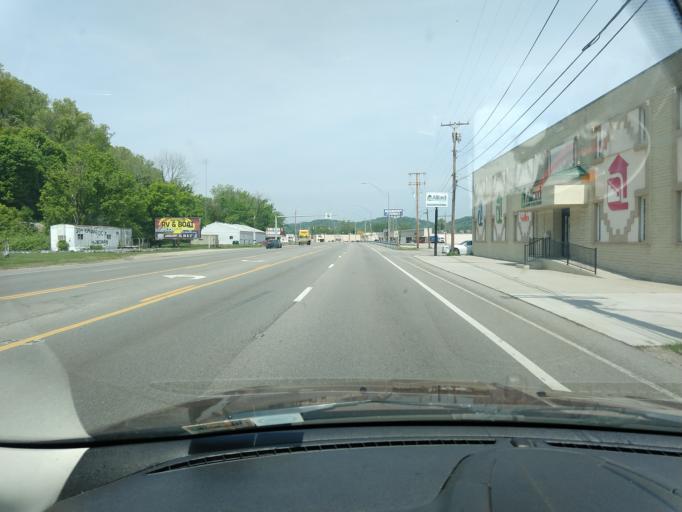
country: US
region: West Virginia
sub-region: Kanawha County
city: Dunbar
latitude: 38.3671
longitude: -81.7648
